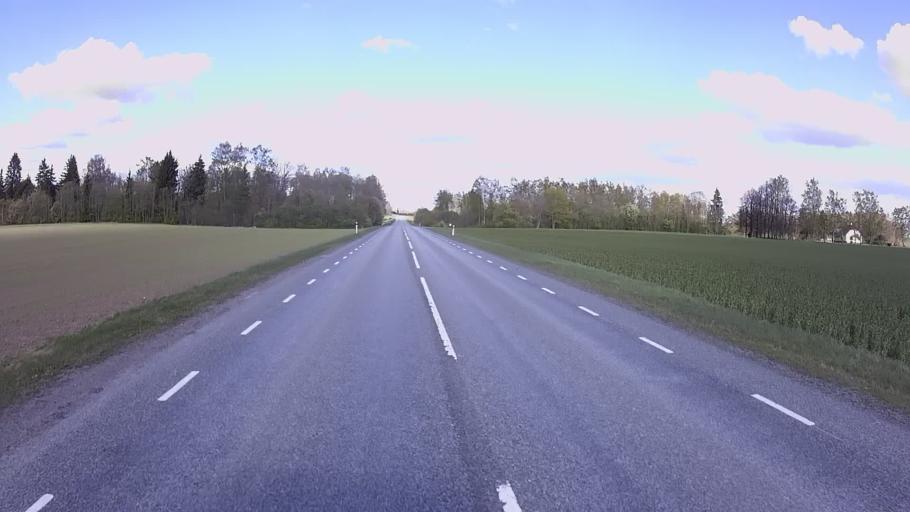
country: EE
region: Jogevamaa
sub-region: Poltsamaa linn
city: Poltsamaa
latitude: 58.6818
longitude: 26.0683
